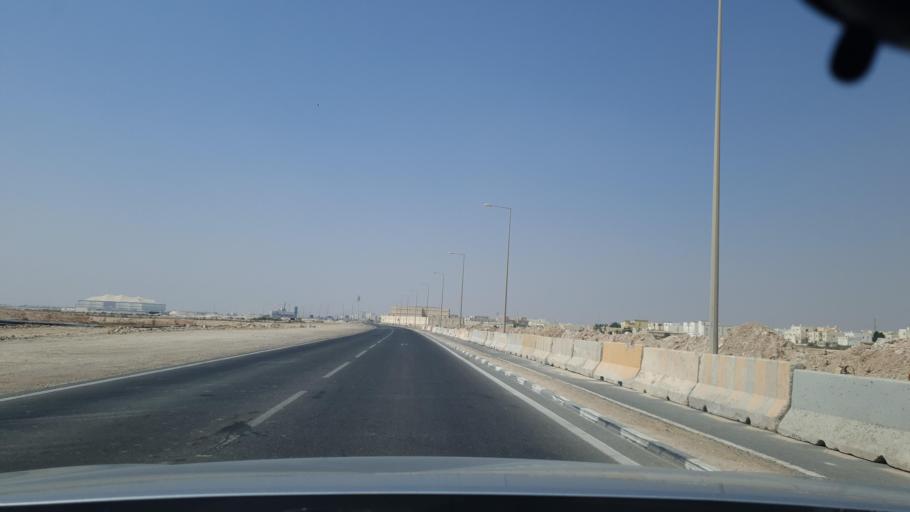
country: QA
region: Al Khawr
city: Al Khawr
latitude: 25.6677
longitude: 51.5231
